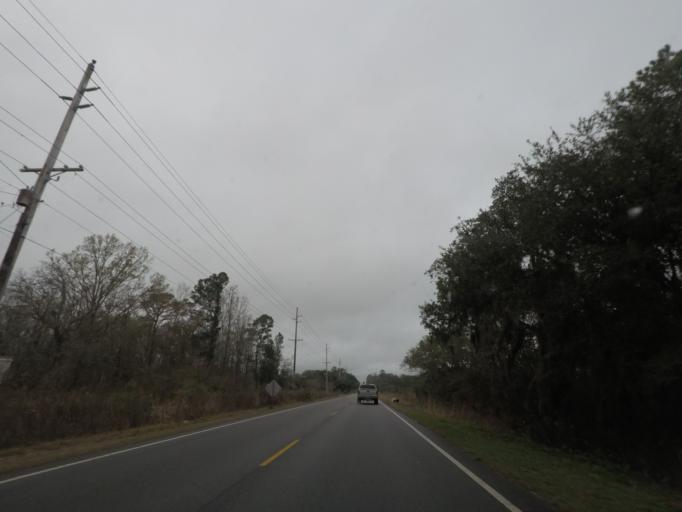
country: US
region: South Carolina
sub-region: Charleston County
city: Meggett
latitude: 32.6667
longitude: -80.3431
